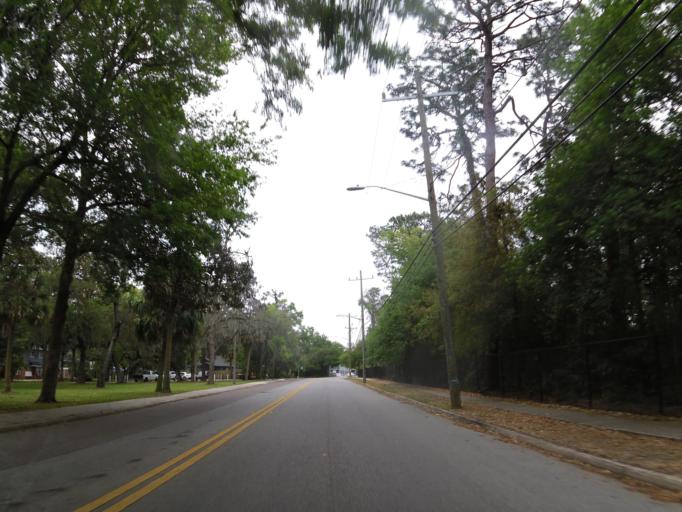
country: US
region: Florida
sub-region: Duval County
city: Jacksonville
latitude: 30.3008
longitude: -81.6329
